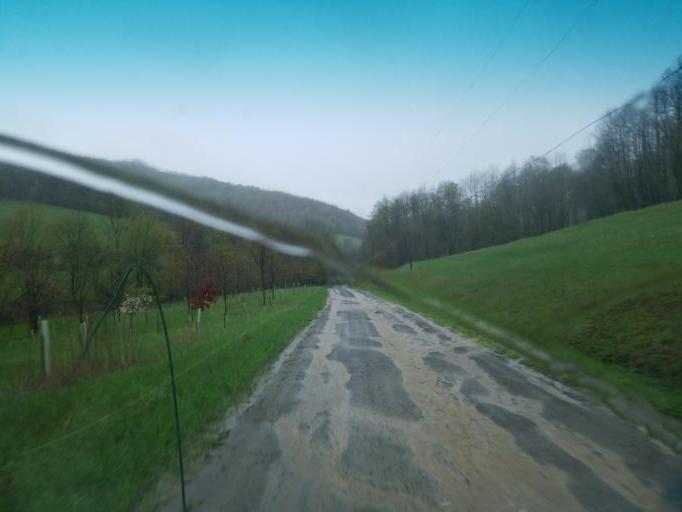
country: US
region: Pennsylvania
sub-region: Tioga County
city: Westfield
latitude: 41.9139
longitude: -77.6449
